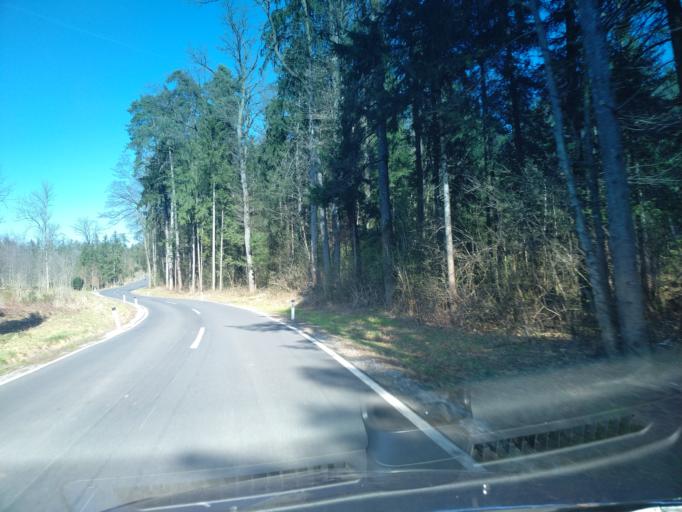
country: AT
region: Styria
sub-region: Politischer Bezirk Graz-Umgebung
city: Wundschuh
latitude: 46.9157
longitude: 15.4193
